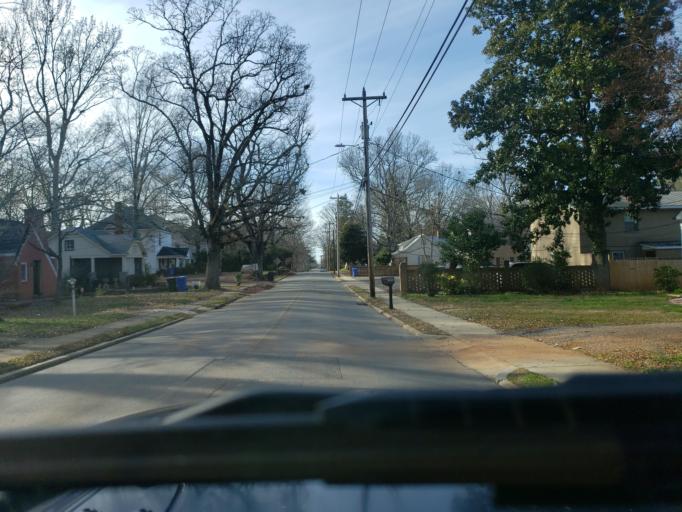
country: US
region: North Carolina
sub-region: Cleveland County
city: Kings Mountain
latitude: 35.2381
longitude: -81.3475
